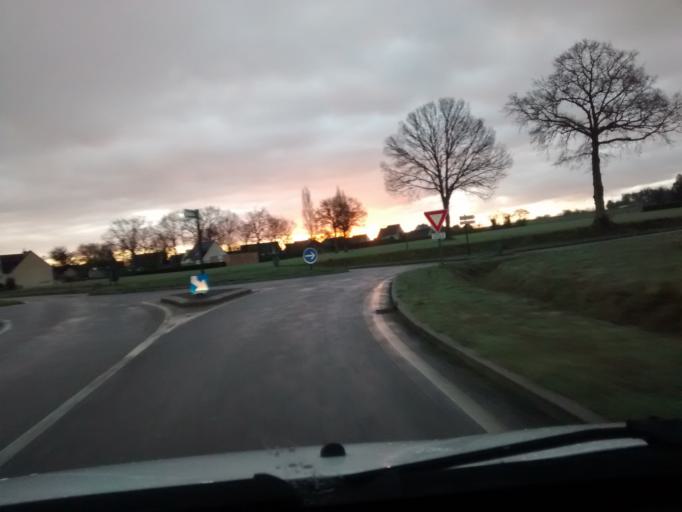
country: FR
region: Brittany
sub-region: Departement d'Ille-et-Vilaine
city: Saint-Didier
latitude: 48.0956
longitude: -1.3826
